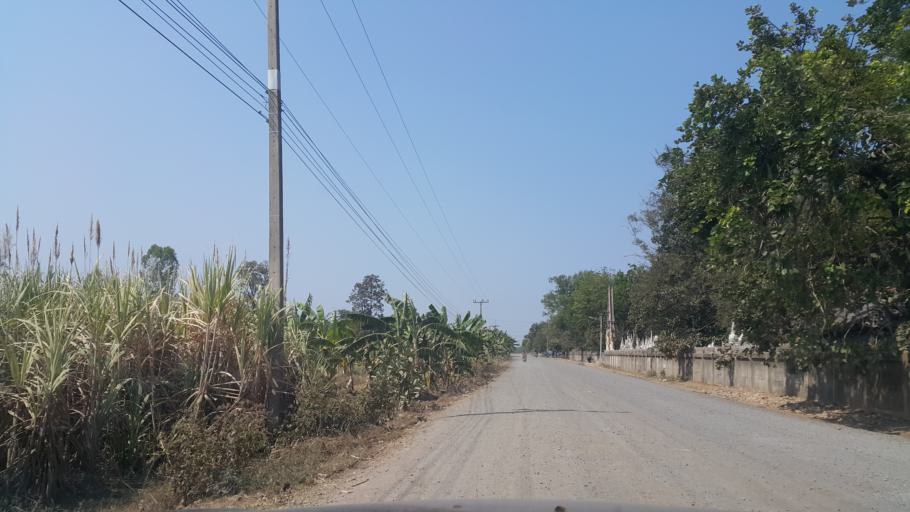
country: TH
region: Buriram
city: Satuek
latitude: 15.1326
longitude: 103.3516
